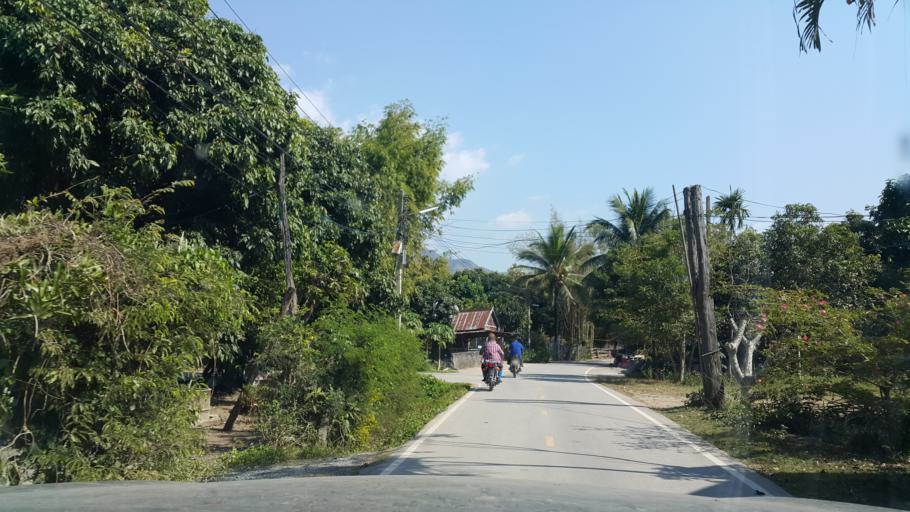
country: TH
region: Chiang Mai
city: Mae On
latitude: 18.7294
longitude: 99.2099
